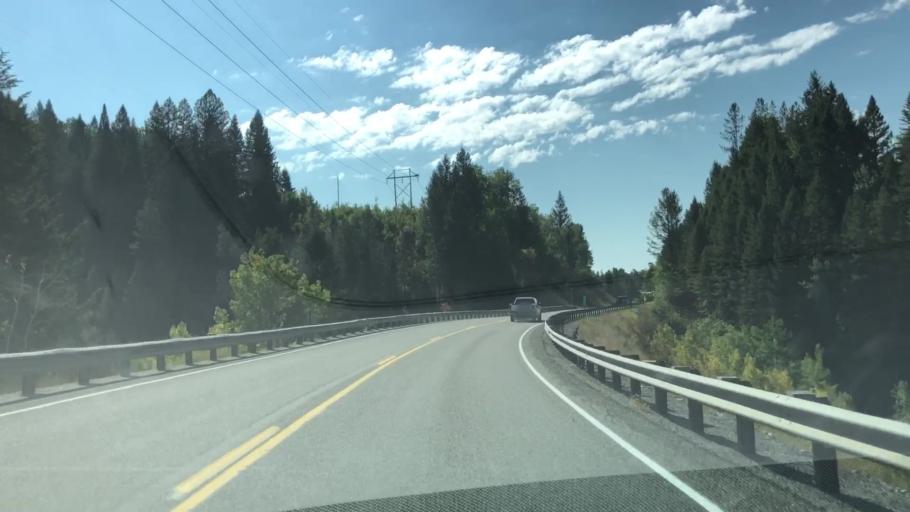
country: US
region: Idaho
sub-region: Teton County
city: Victor
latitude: 43.2999
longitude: -111.1297
